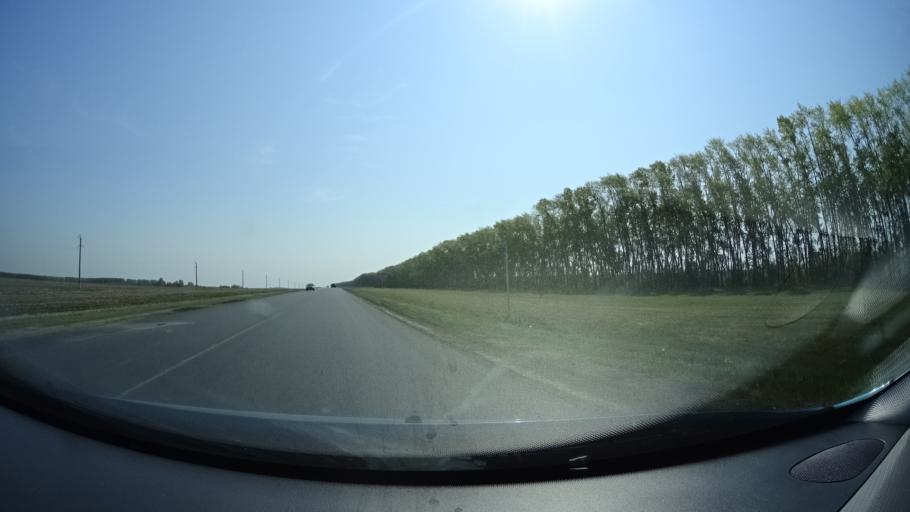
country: RU
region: Bashkortostan
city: Karmaskaly
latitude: 54.4120
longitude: 56.0639
